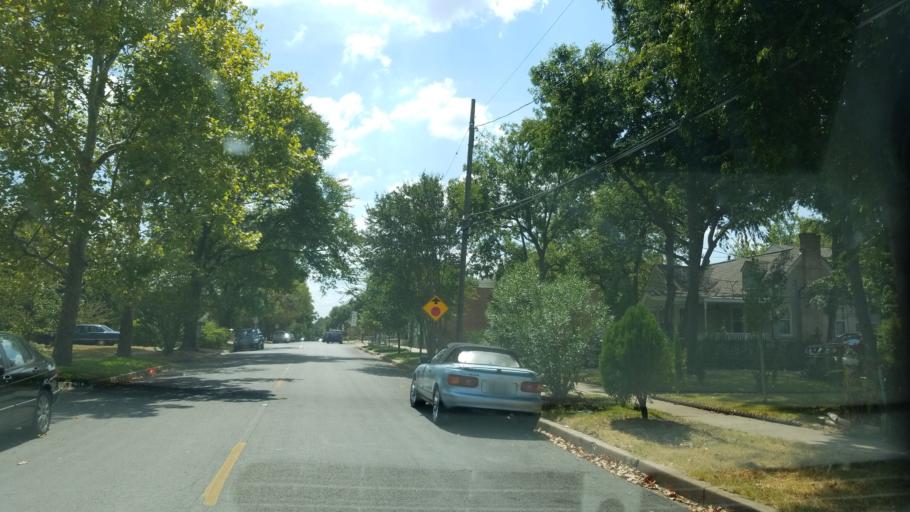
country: US
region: Texas
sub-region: Dallas County
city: Cockrell Hill
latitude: 32.7531
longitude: -96.8465
